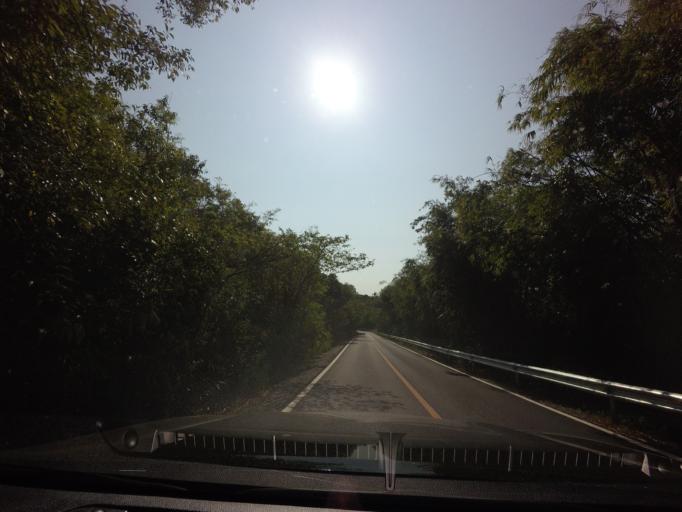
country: TH
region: Kanchanaburi
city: Thong Pha Phum
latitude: 14.6908
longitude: 98.4074
